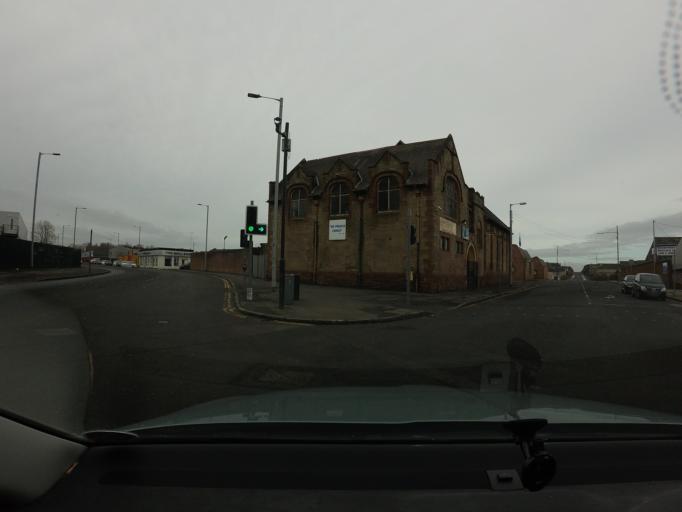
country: GB
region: Scotland
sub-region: South Lanarkshire
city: Rutherglen
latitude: 55.8350
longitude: -4.2447
